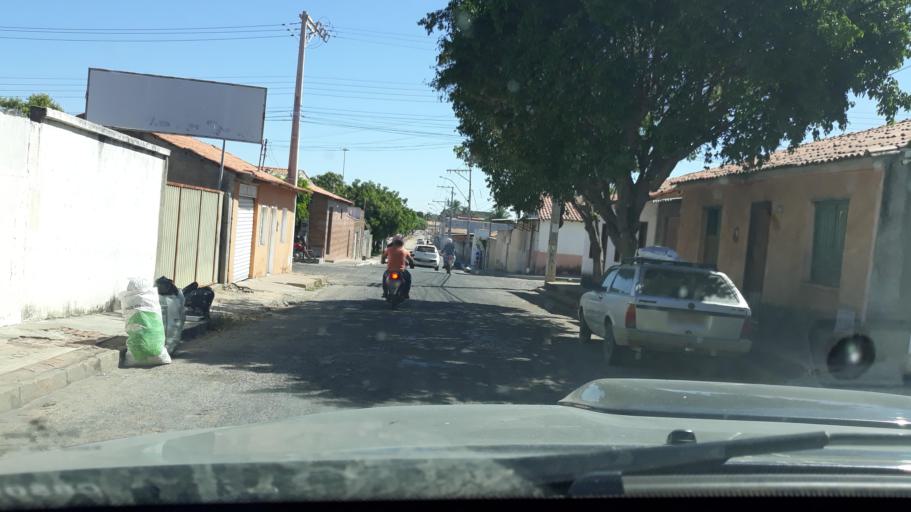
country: BR
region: Bahia
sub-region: Guanambi
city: Guanambi
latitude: -14.2257
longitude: -42.7870
